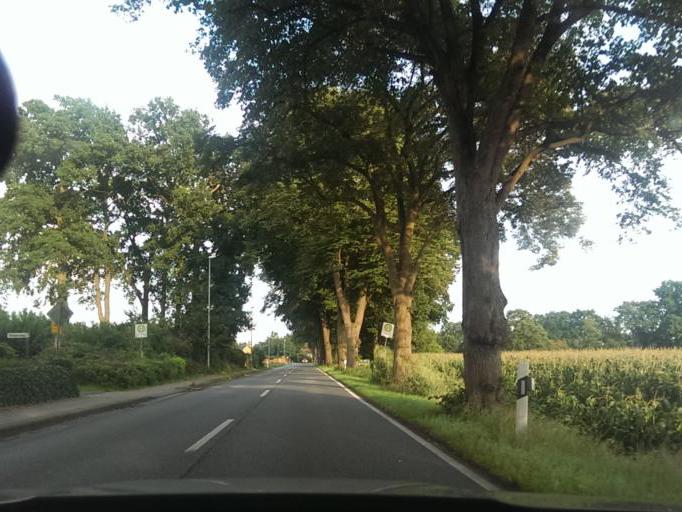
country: DE
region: Lower Saxony
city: Lilienthal
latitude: 53.1712
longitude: 8.9232
